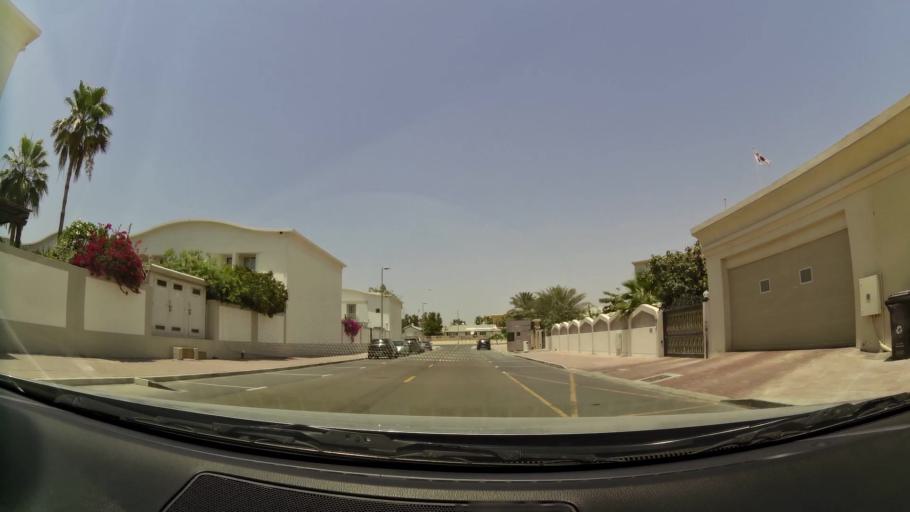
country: AE
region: Dubai
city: Dubai
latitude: 25.1990
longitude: 55.2460
